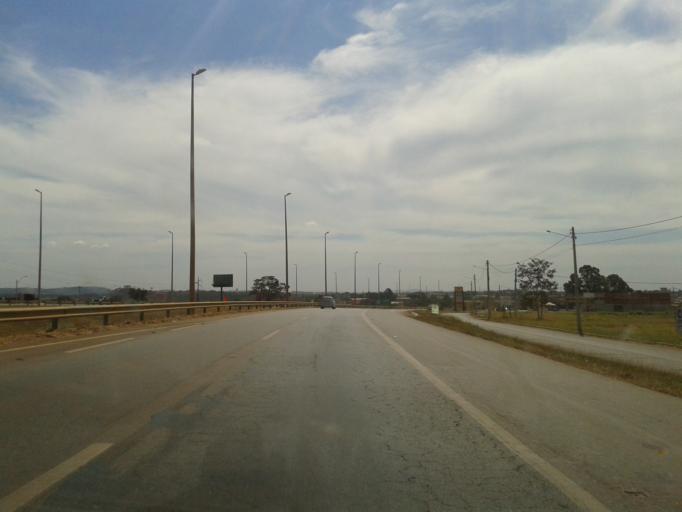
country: BR
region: Goias
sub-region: Goianira
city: Goianira
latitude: -16.5548
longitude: -49.4064
